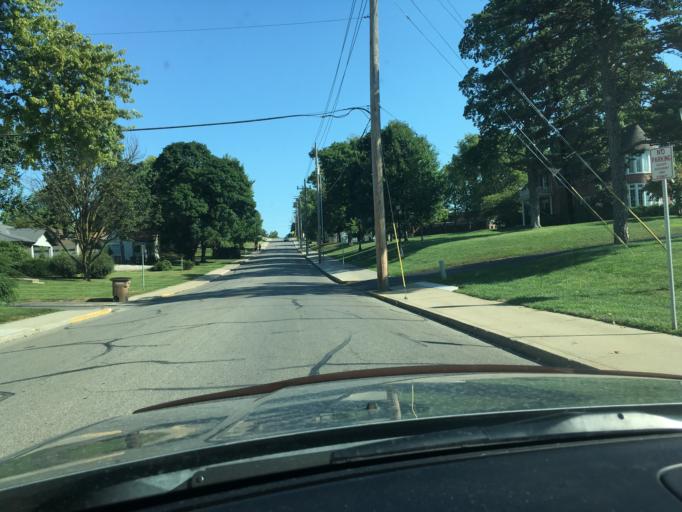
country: US
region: Kansas
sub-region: Atchison County
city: Atchison
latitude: 39.5739
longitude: -95.1152
